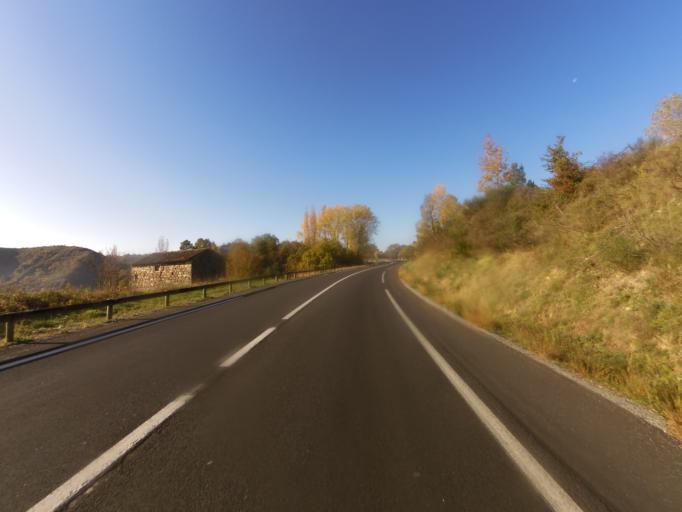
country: FR
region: Rhone-Alpes
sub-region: Departement de l'Ardeche
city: Joyeuse
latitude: 44.4707
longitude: 4.2343
